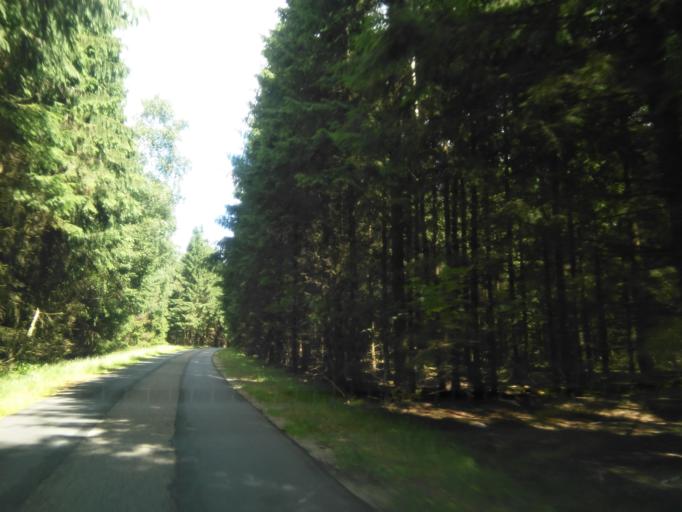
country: DK
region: Central Jutland
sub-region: Silkeborg Kommune
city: Virklund
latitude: 56.0357
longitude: 9.4167
